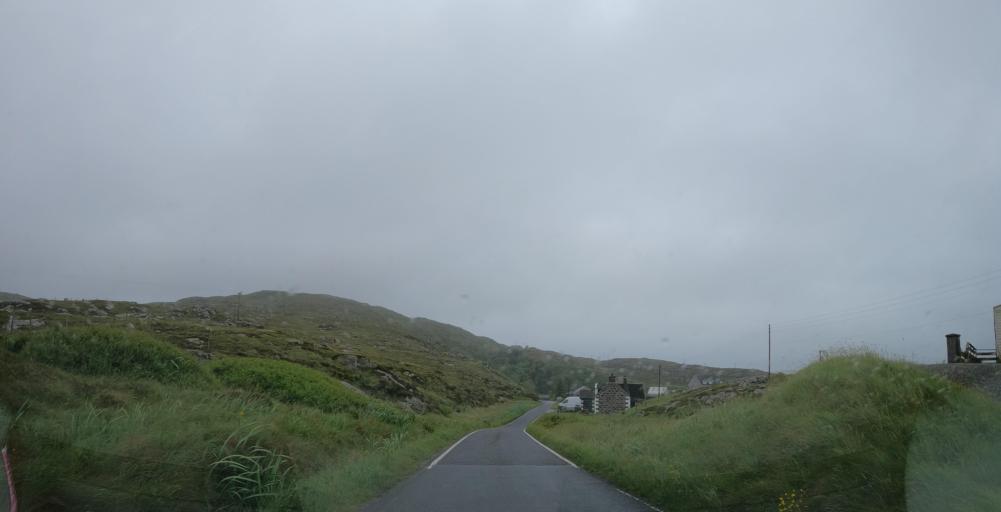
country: GB
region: Scotland
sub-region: Eilean Siar
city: Barra
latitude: 57.0099
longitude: -7.4301
